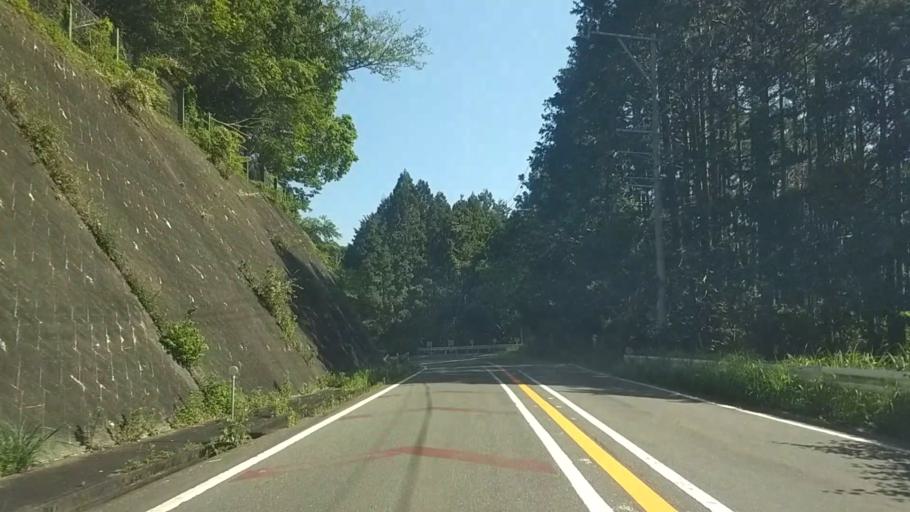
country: JP
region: Shizuoka
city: Fujinomiya
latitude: 35.1865
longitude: 138.5291
